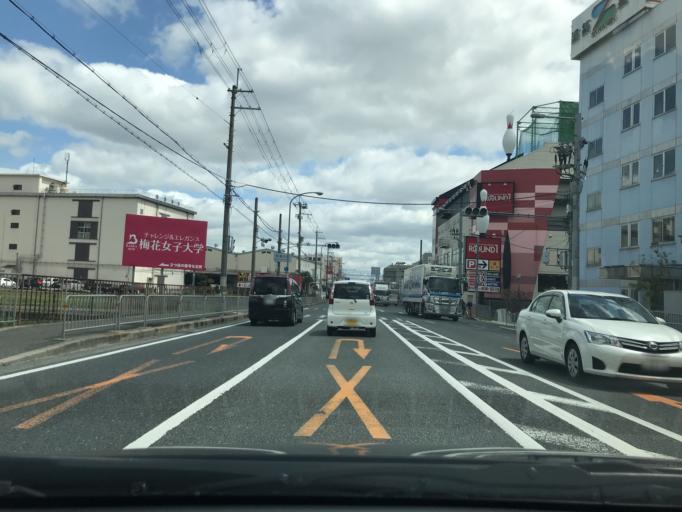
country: JP
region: Osaka
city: Ibaraki
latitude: 34.8363
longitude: 135.5320
